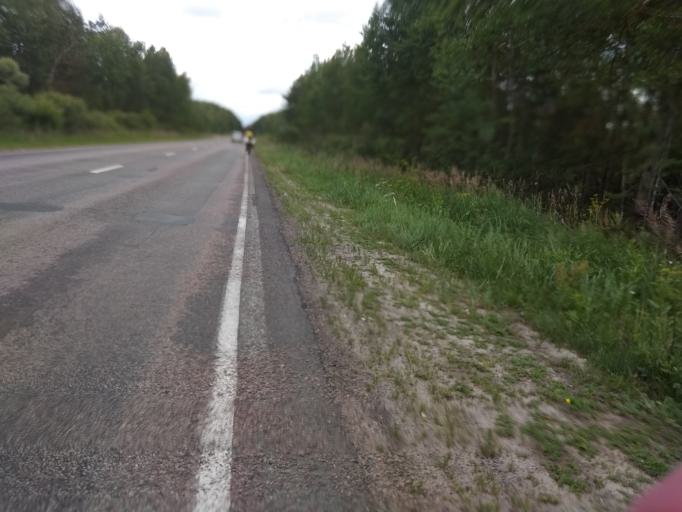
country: RU
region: Moskovskaya
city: Misheronskiy
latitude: 55.6071
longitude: 39.7118
